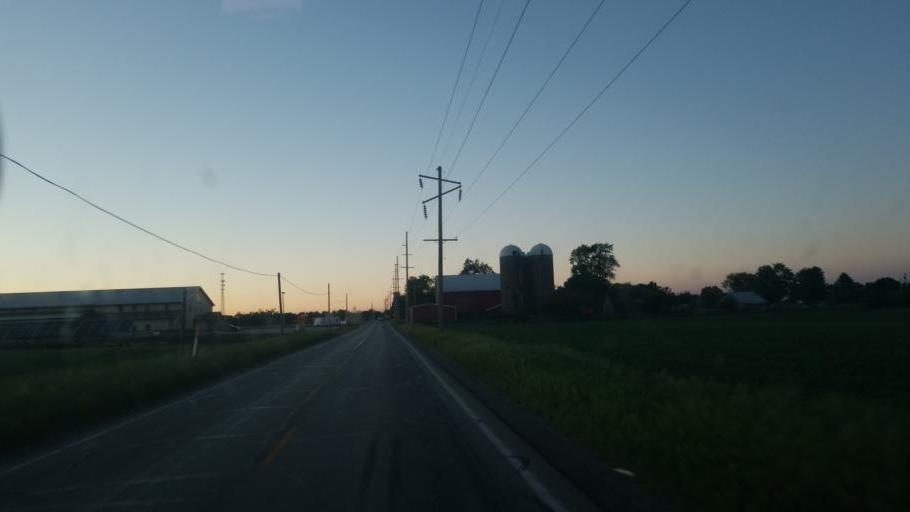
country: US
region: Indiana
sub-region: Elkhart County
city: Nappanee
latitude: 41.4247
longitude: -86.0006
